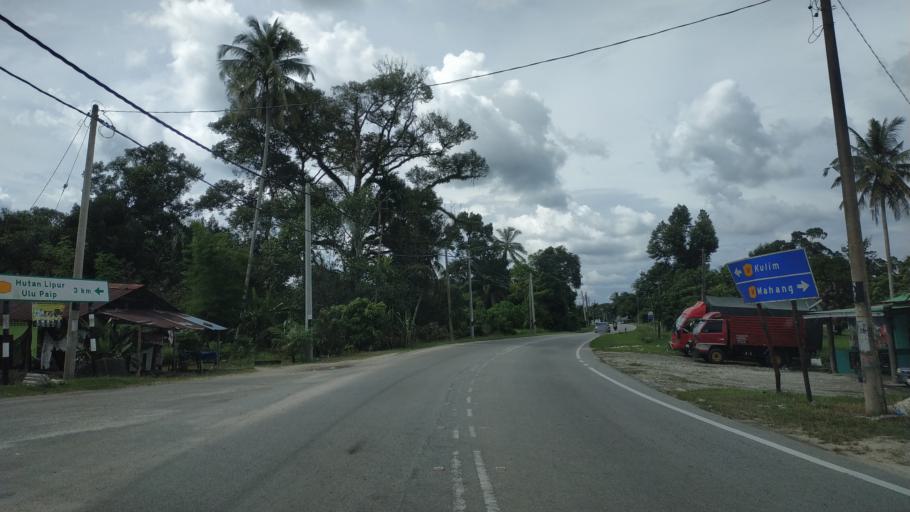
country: MY
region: Kedah
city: Kulim
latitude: 5.4220
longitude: 100.6656
